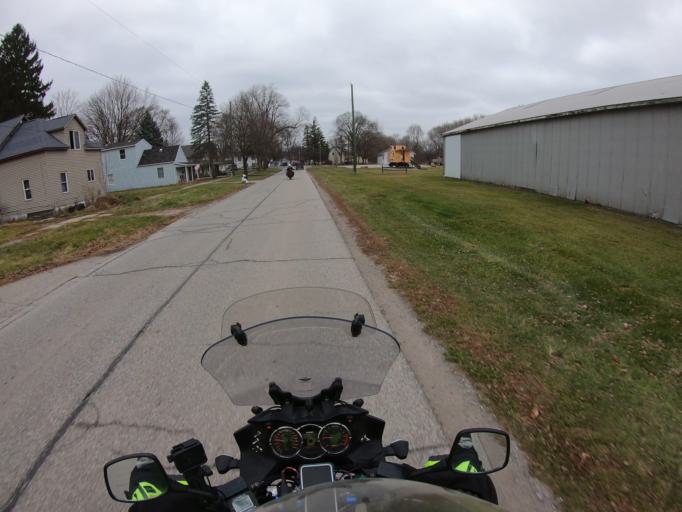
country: US
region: Michigan
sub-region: Saginaw County
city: Saint Charles
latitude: 43.2931
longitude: -84.1370
